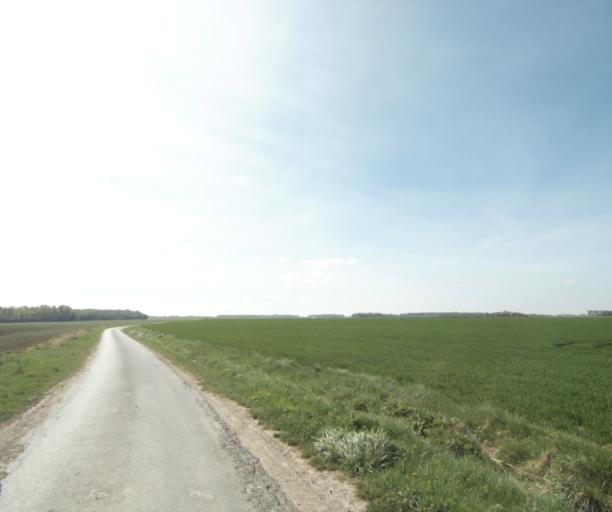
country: FR
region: Ile-de-France
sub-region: Departement de Seine-et-Marne
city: Nangis
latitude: 48.5460
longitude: 3.0356
